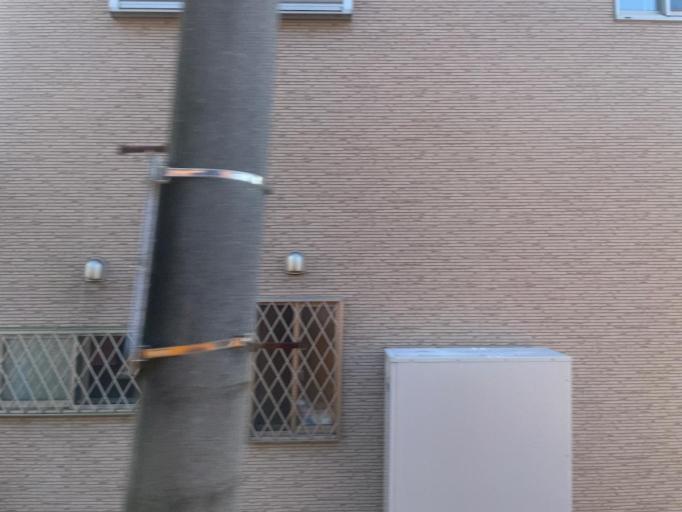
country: JP
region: Mie
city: Toba
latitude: 34.4670
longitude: 136.8405
